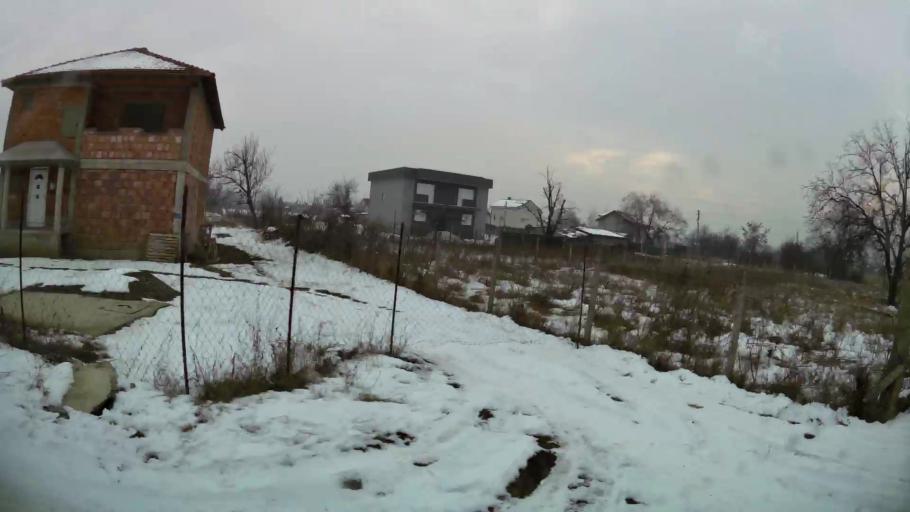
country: MK
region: Saraj
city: Saraj
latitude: 42.0389
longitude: 21.3520
